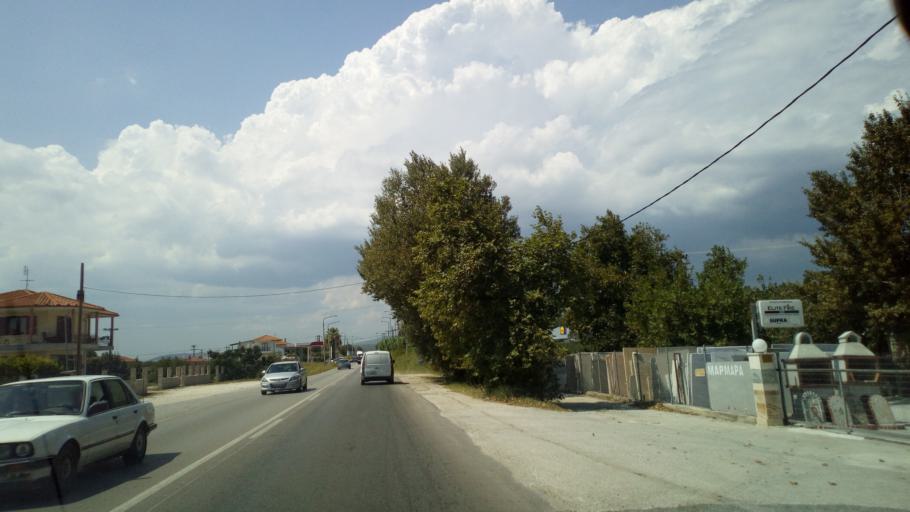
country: GR
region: Central Macedonia
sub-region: Nomos Chalkidikis
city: Nikiti
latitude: 40.2150
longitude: 23.6805
